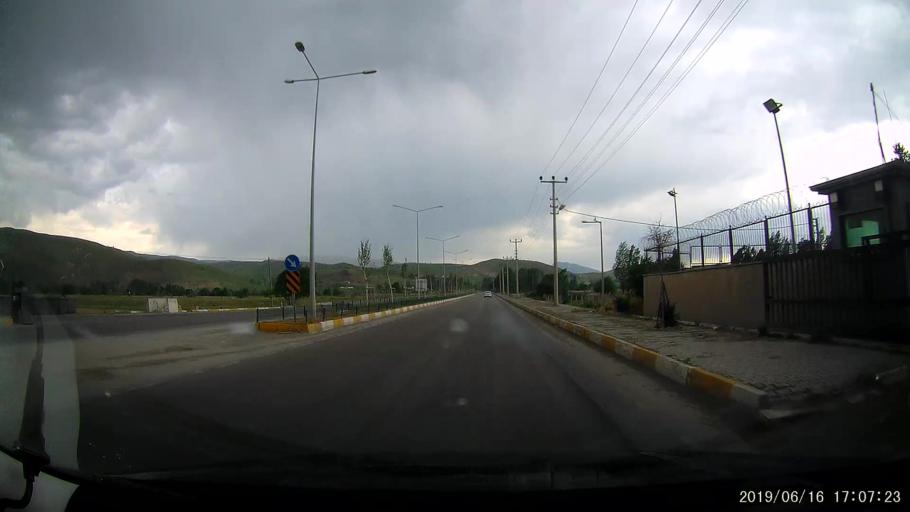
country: TR
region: Erzurum
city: Askale
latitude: 39.9178
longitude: 40.6773
